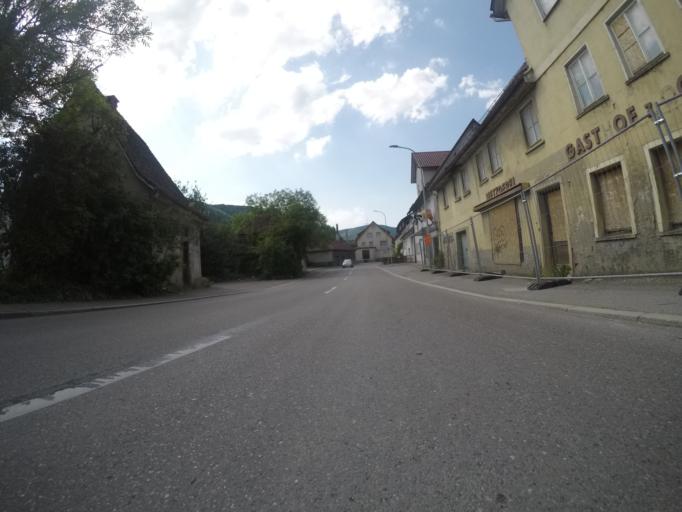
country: DE
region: Baden-Wuerttemberg
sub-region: Tuebingen Region
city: Grabenstetten
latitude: 48.5498
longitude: 9.4713
